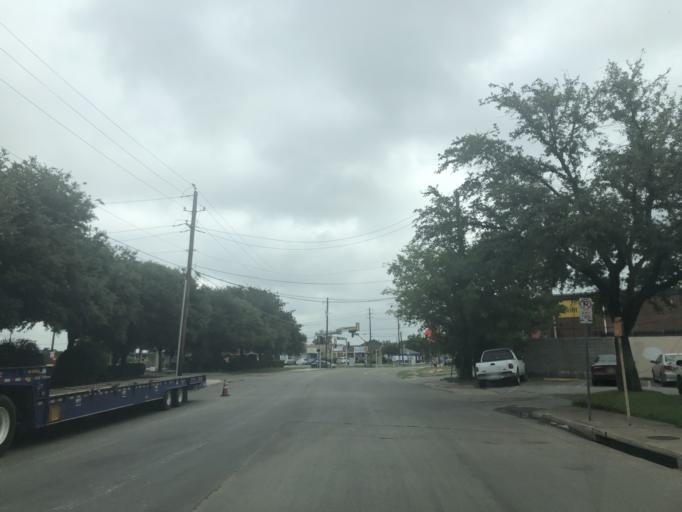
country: US
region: Texas
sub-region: Dallas County
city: University Park
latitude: 32.8641
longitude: -96.8629
